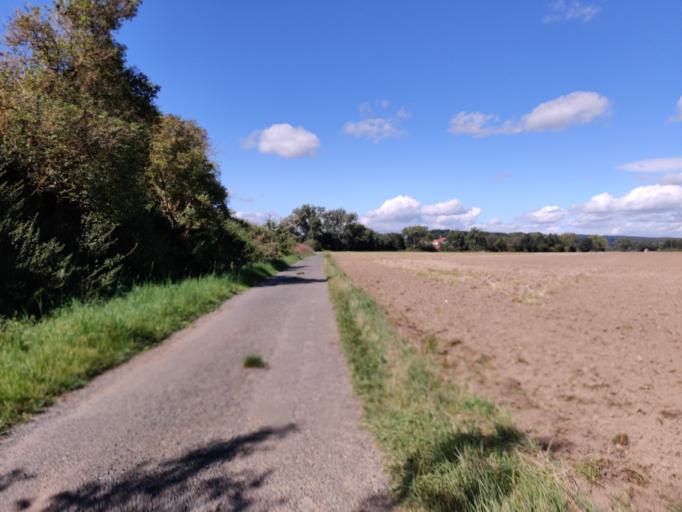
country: DE
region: Lower Saxony
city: Baddeckenstedt
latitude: 52.0899
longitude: 10.2094
